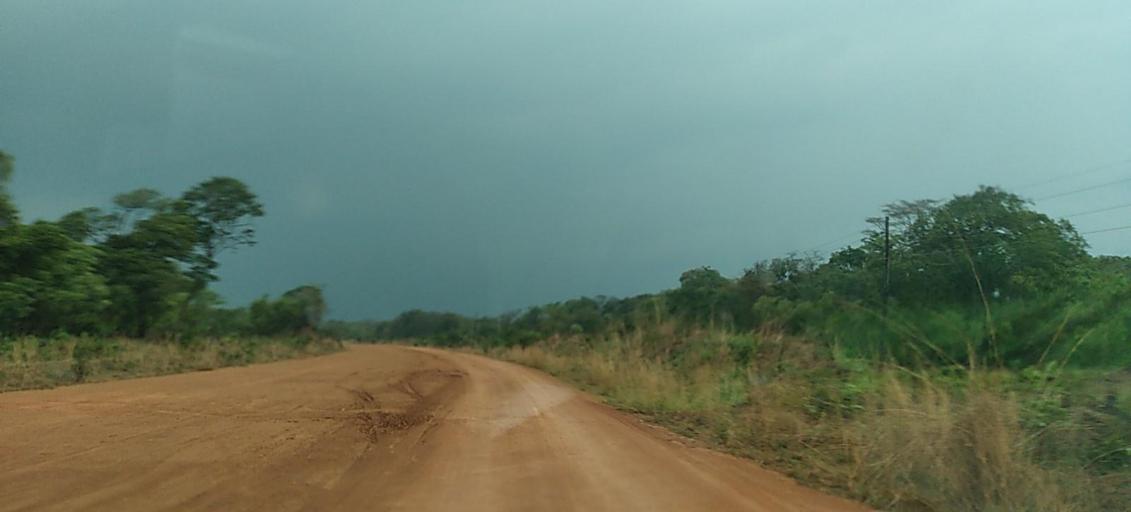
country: ZM
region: North-Western
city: Mwinilunga
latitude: -11.6404
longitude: 24.3993
